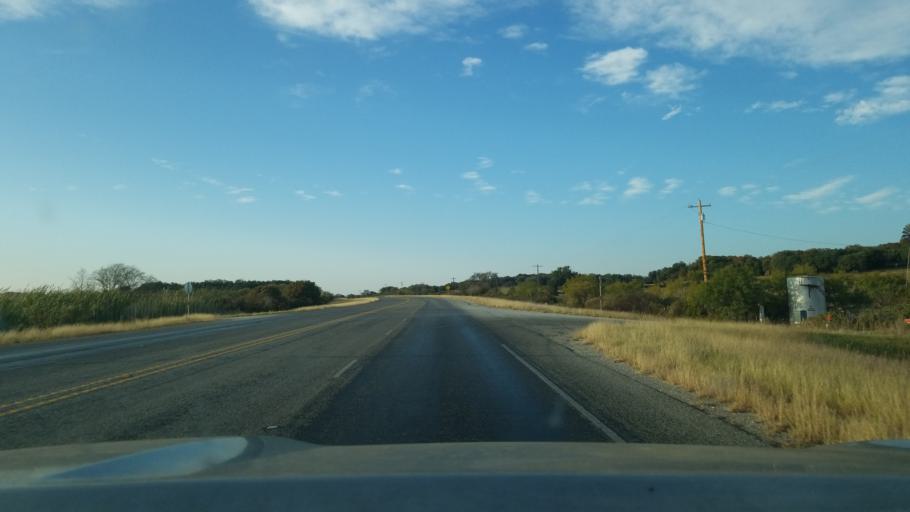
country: US
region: Texas
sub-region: Brown County
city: Lake Brownwood
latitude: 32.0622
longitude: -98.9494
